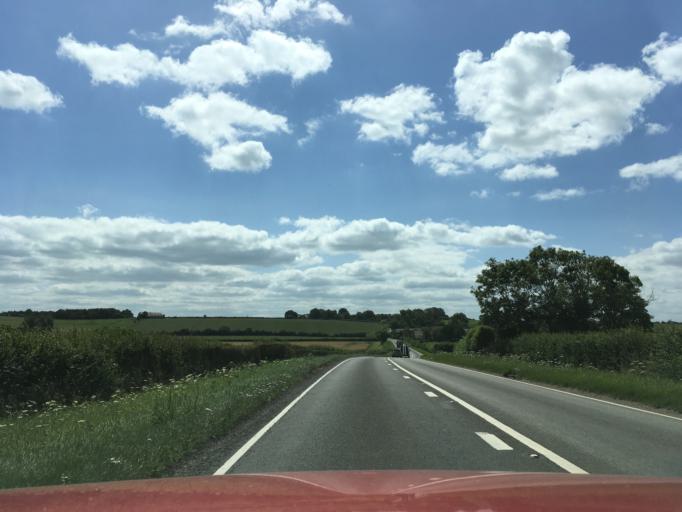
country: GB
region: England
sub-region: Buckinghamshire
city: Winslow
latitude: 51.9031
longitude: -0.8345
